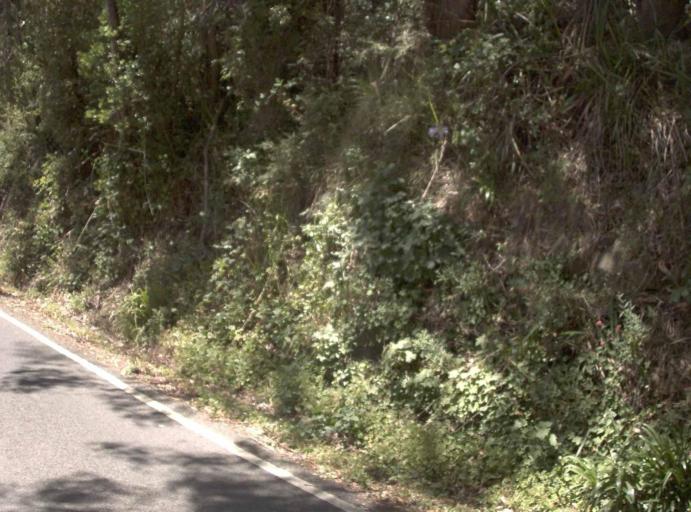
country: AU
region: Victoria
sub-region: Yarra Ranges
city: Olinda
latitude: -37.8521
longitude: 145.3620
